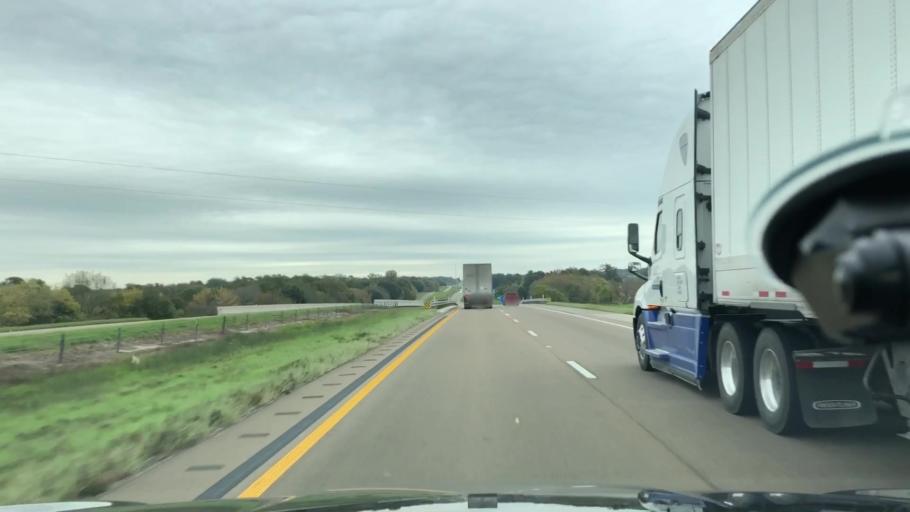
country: US
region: Texas
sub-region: Titus County
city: Mount Pleasant
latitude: 33.1631
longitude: -95.0210
